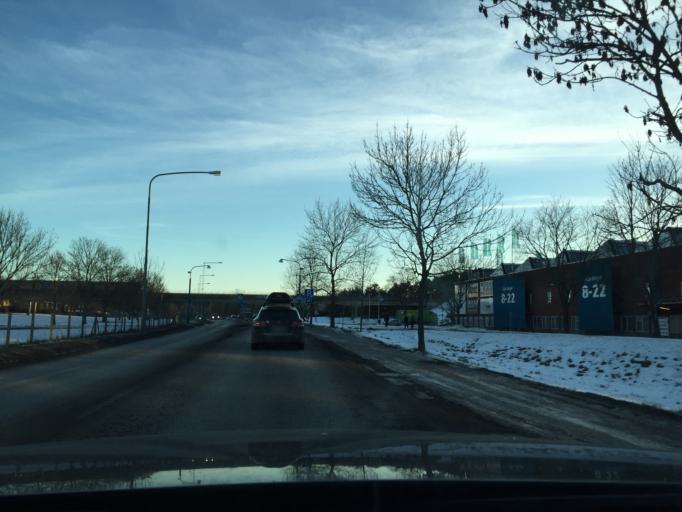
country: SE
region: Stockholm
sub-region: Jarfalla Kommun
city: Jakobsberg
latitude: 59.3696
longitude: 17.8610
